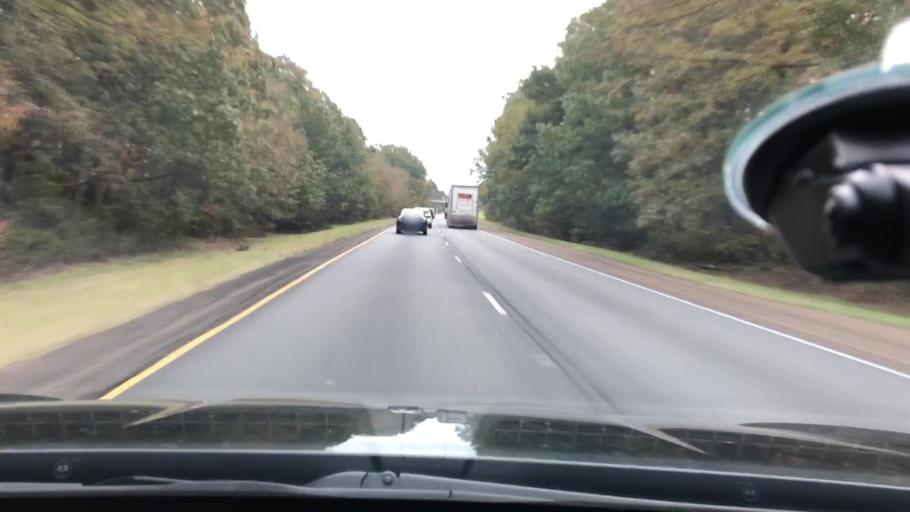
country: US
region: Arkansas
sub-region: Nevada County
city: Prescott
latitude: 33.8460
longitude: -93.3766
